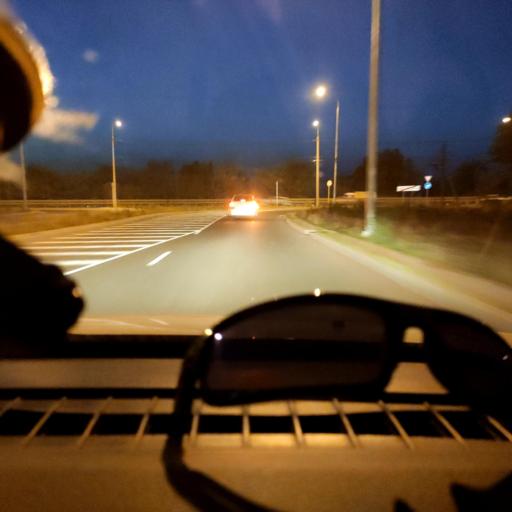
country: RU
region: Samara
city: Samara
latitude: 53.1010
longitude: 50.1624
